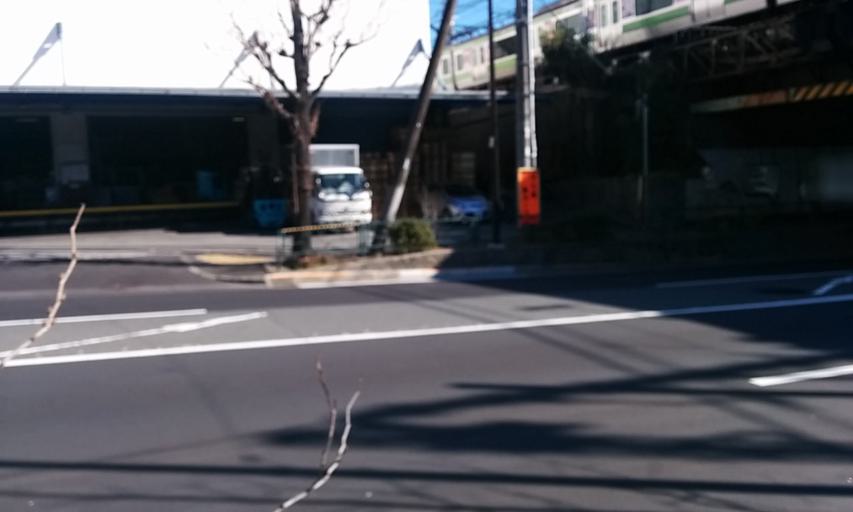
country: JP
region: Tokyo
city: Tokyo
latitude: 35.6175
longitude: 139.7348
